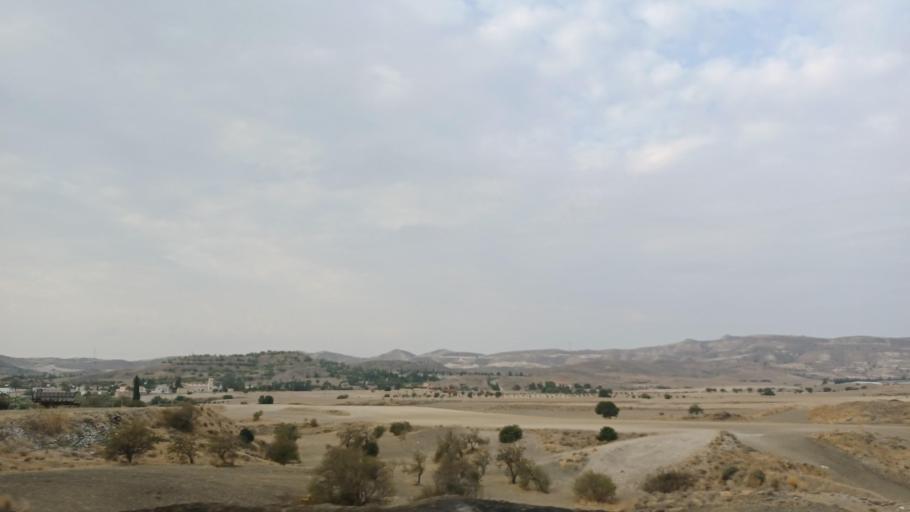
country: CY
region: Larnaka
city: Troulloi
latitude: 35.0148
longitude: 33.5728
